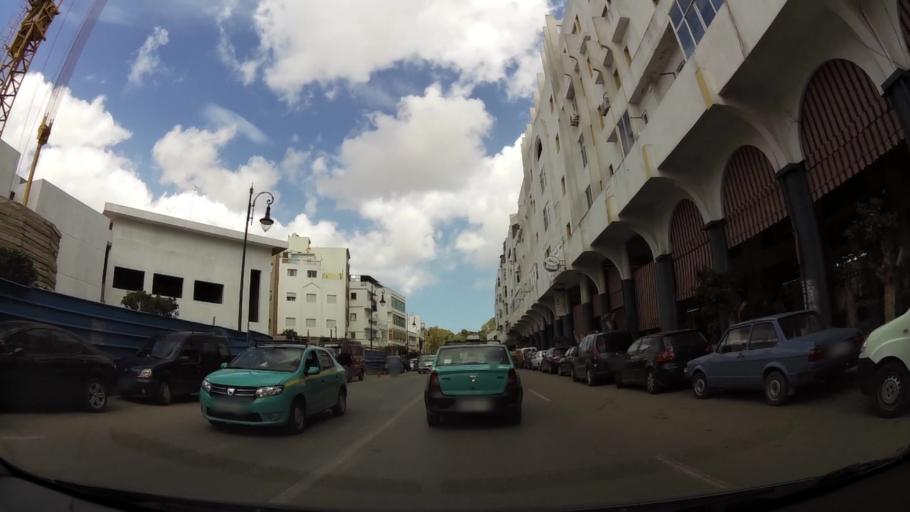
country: MA
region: Tanger-Tetouan
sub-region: Tanger-Assilah
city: Tangier
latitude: 35.7553
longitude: -5.8106
